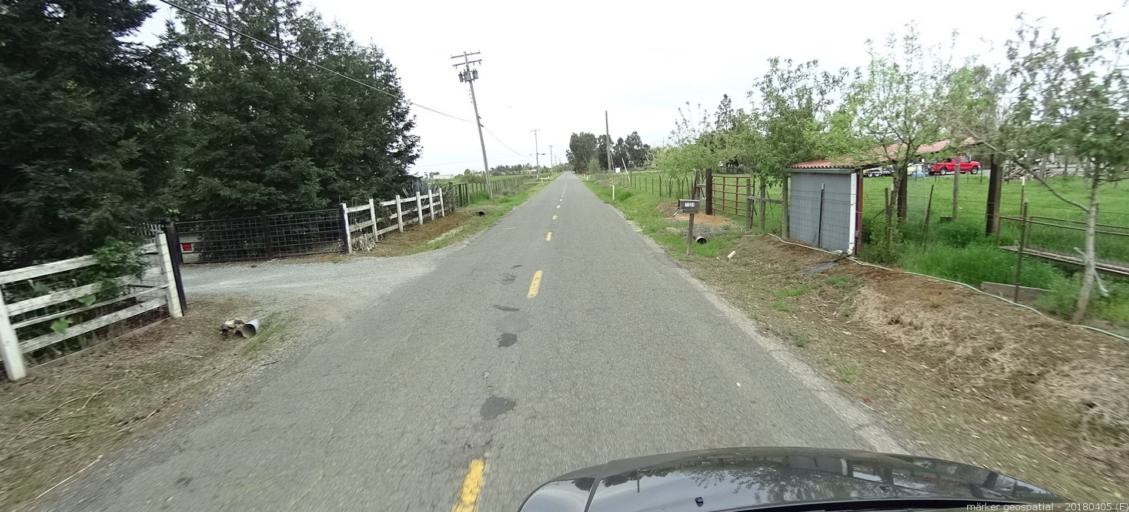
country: US
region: California
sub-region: Sacramento County
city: Herald
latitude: 38.2774
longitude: -121.2344
